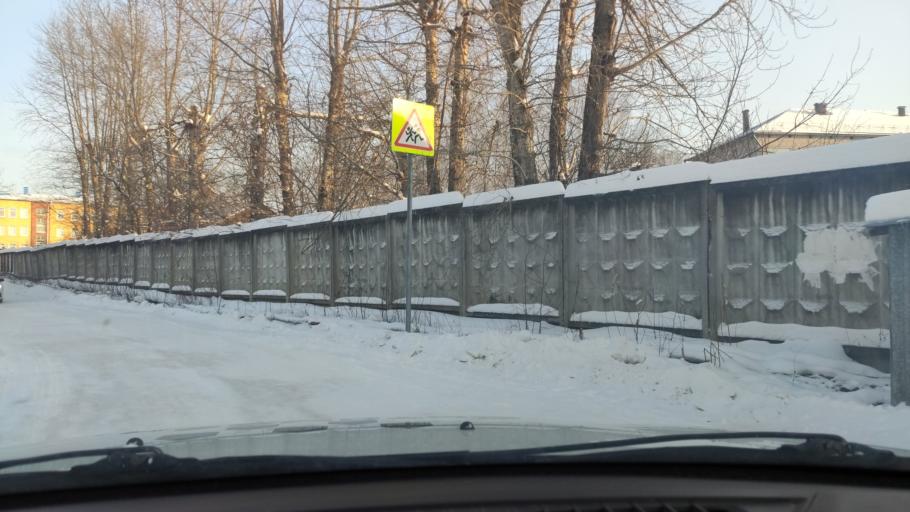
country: RU
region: Perm
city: Froly
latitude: 57.9741
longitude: 56.3123
